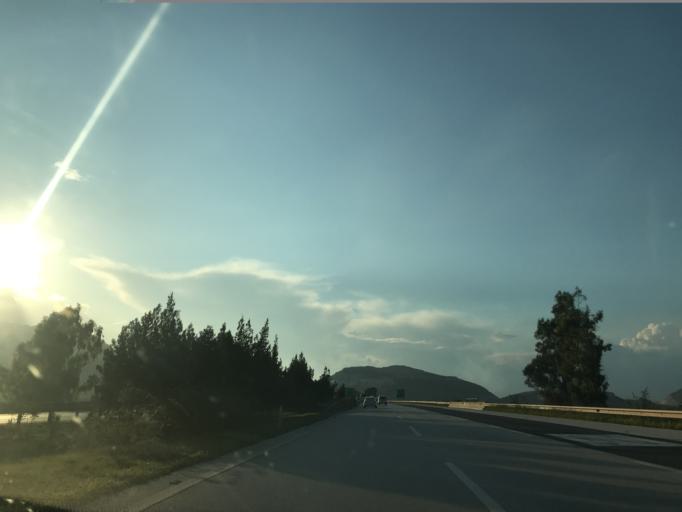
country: TR
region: Adana
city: Ceyhan
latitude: 36.9863
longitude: 35.7646
